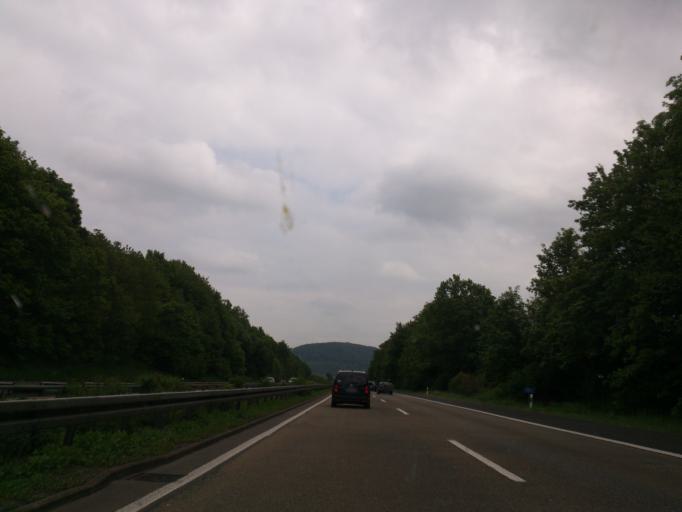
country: DE
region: Hesse
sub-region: Regierungsbezirk Kassel
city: Martinhagen
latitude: 51.2961
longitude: 9.3384
